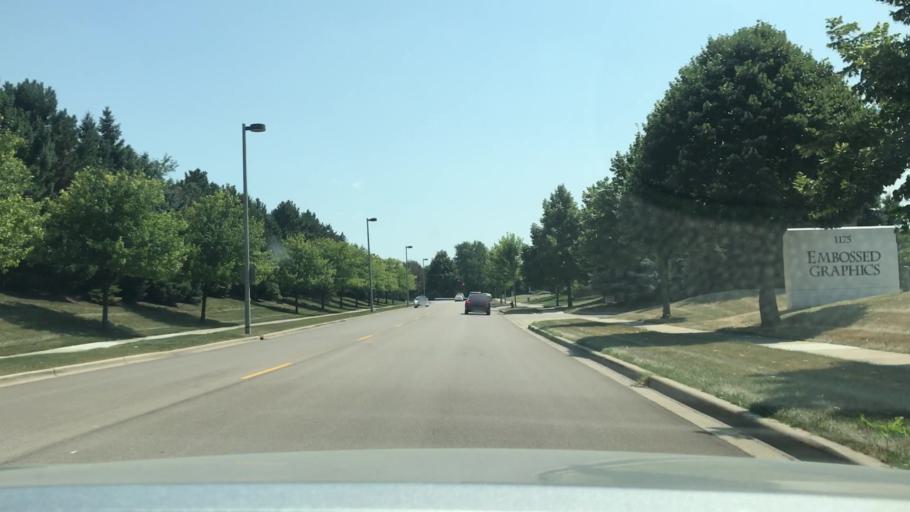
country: US
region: Illinois
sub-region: Kane County
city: Aurora
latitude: 41.7342
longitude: -88.2304
